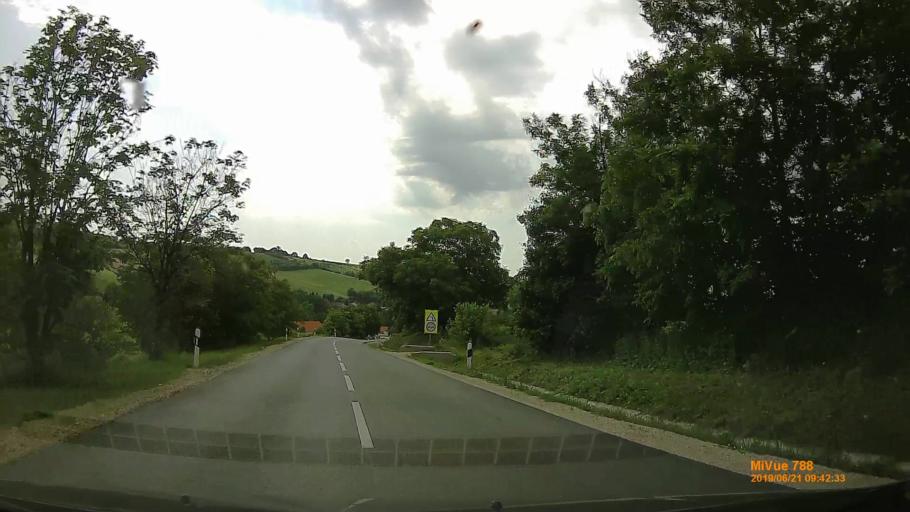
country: HU
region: Somogy
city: Taszar
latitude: 46.2875
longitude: 17.9681
